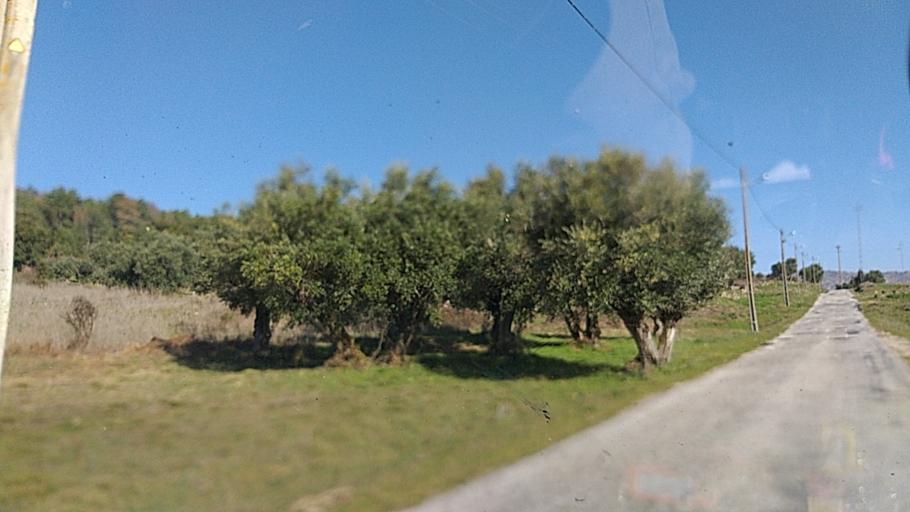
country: PT
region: Guarda
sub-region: Celorico da Beira
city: Celorico da Beira
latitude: 40.6888
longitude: -7.4542
